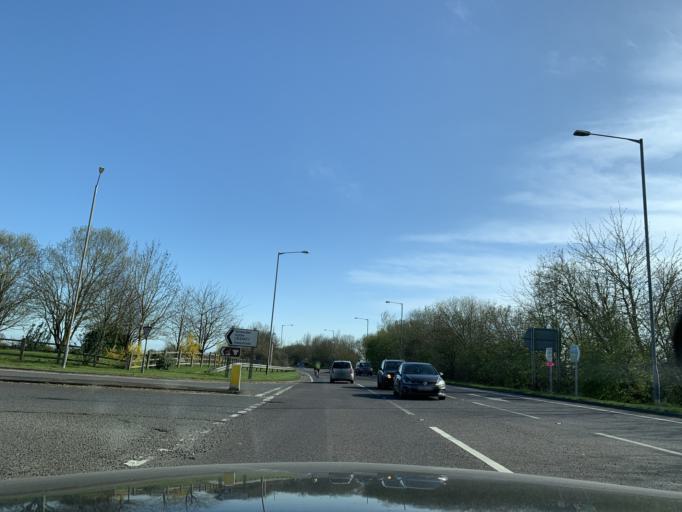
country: GB
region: England
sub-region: Kent
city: Romney Marsh
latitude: 51.0504
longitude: 0.8546
